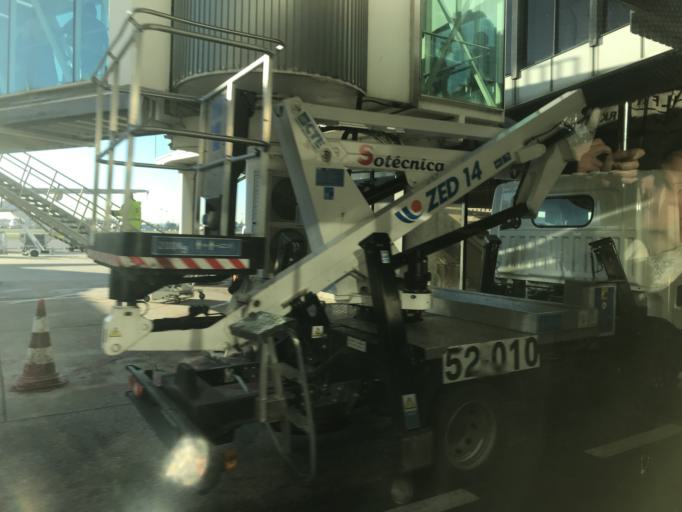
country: PT
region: Lisbon
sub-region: Loures
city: Moscavide
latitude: 38.7687
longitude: -9.1302
